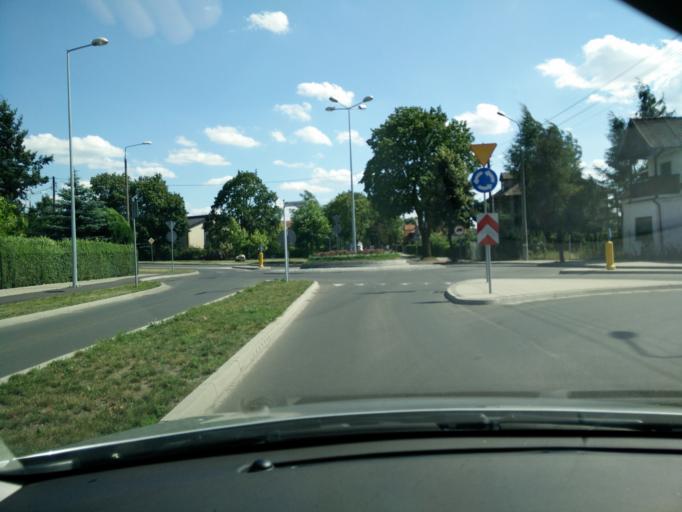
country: PL
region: Greater Poland Voivodeship
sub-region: Powiat sredzki
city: Sroda Wielkopolska
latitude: 52.2278
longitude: 17.2655
